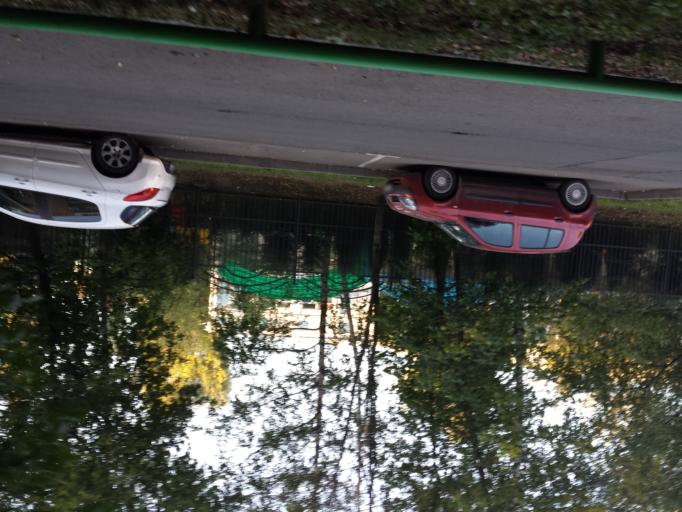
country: RU
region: Moskovskaya
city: Bol'shaya Setun'
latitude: 55.7252
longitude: 37.4422
